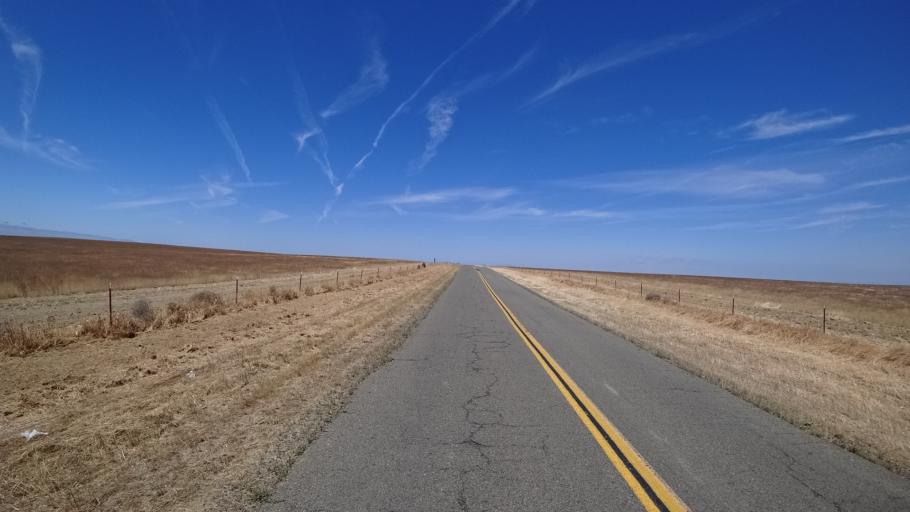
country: US
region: California
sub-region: Kings County
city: Kettleman City
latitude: 35.7996
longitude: -119.8949
